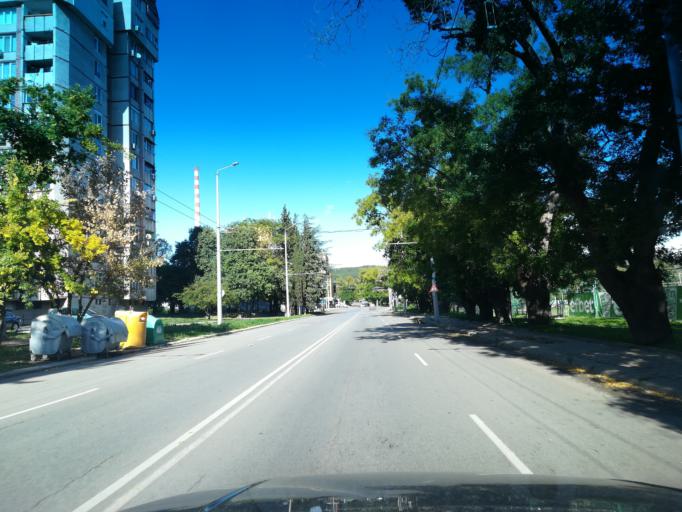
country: BG
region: Stara Zagora
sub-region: Obshtina Stara Zagora
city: Stara Zagora
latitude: 42.4411
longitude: 25.6331
